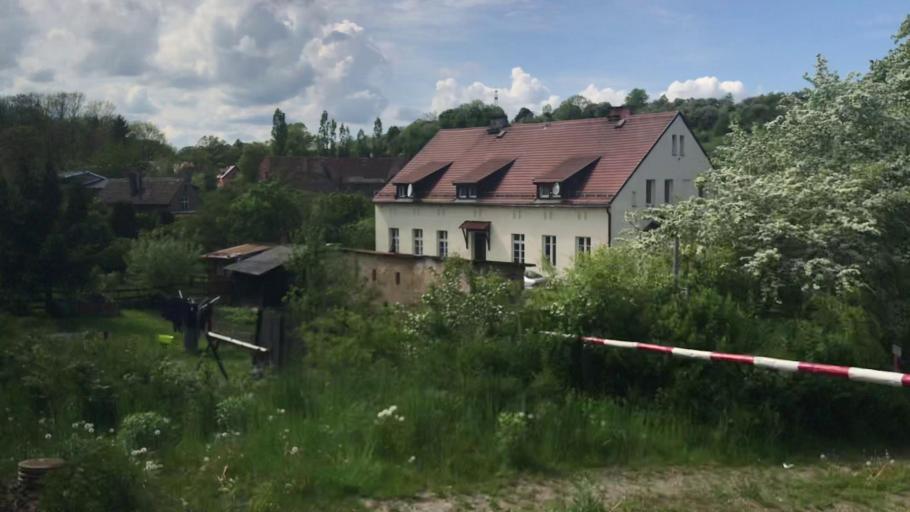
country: PL
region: Lower Silesian Voivodeship
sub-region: Powiat swidnicki
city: Swiebodzice
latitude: 50.8310
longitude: 16.3328
